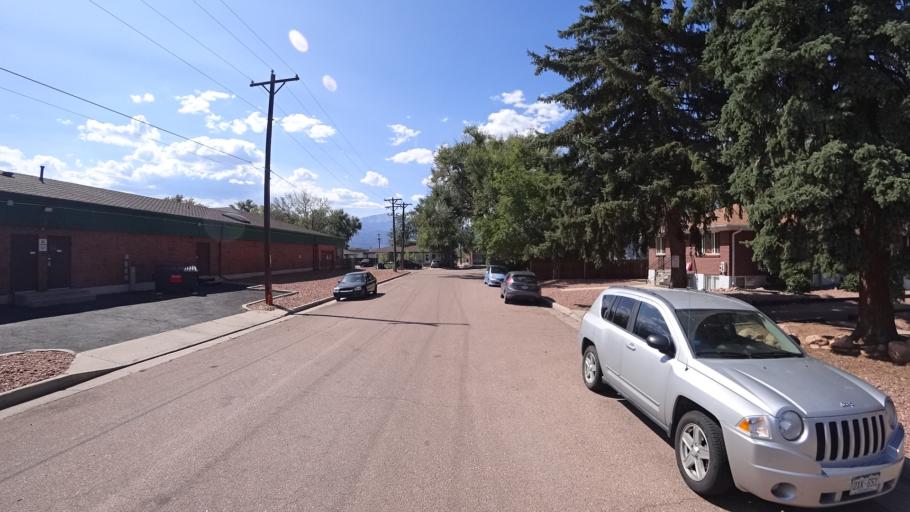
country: US
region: Colorado
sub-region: El Paso County
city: Colorado Springs
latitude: 38.8750
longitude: -104.8091
